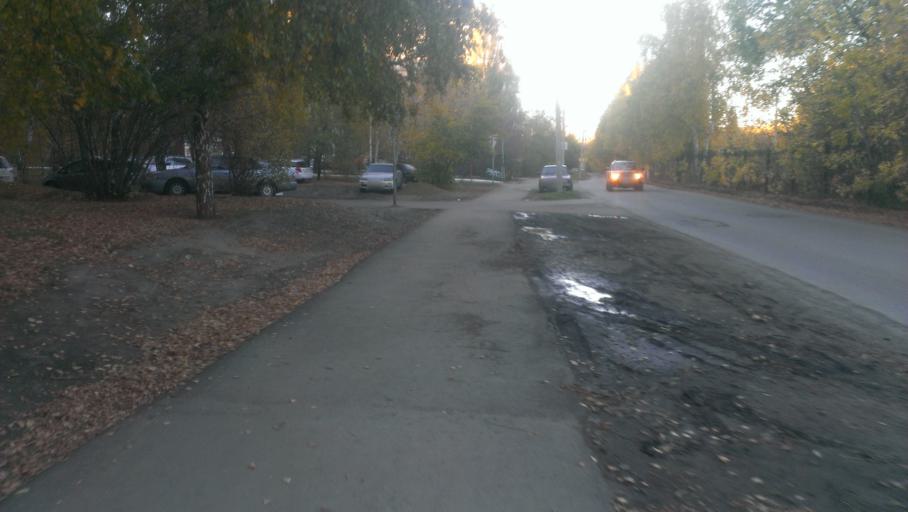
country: RU
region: Altai Krai
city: Novosilikatnyy
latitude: 53.3585
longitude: 83.6790
